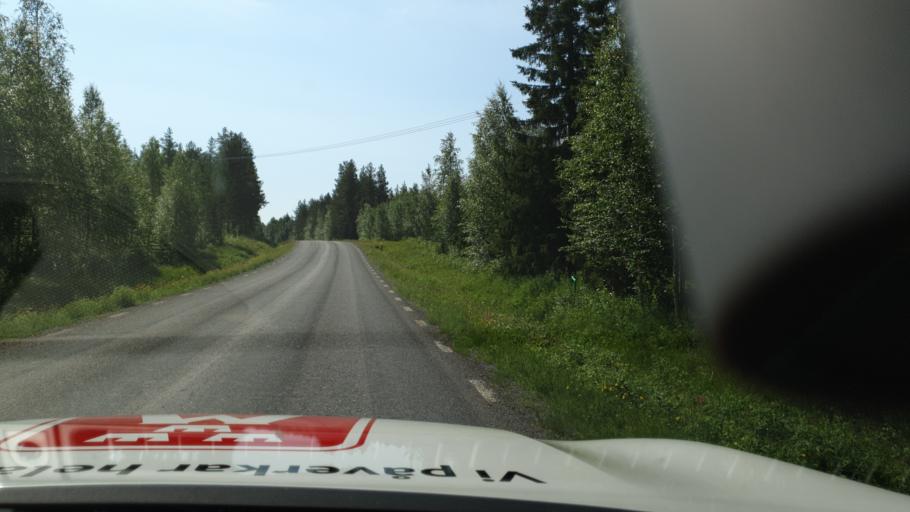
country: SE
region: Vaesterbotten
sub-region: Skelleftea Kommun
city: Langsele
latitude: 65.0190
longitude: 20.0764
